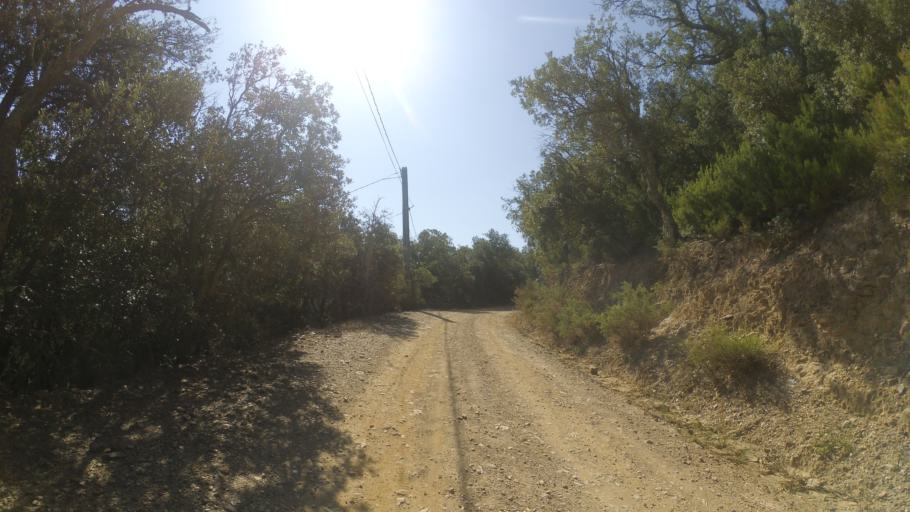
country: FR
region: Languedoc-Roussillon
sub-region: Departement des Pyrenees-Orientales
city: Millas
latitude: 42.6211
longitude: 2.6768
